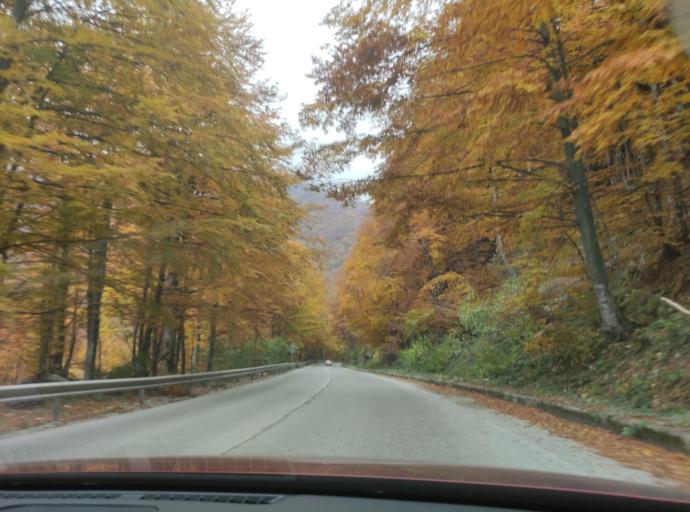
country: BG
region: Montana
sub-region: Obshtina Berkovitsa
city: Berkovitsa
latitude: 43.1301
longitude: 23.1358
